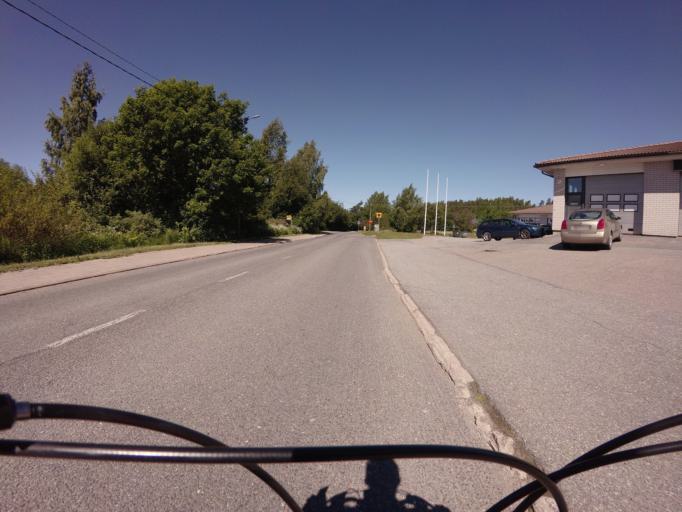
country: FI
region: Varsinais-Suomi
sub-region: Turku
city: Turku
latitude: 60.4579
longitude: 22.2160
